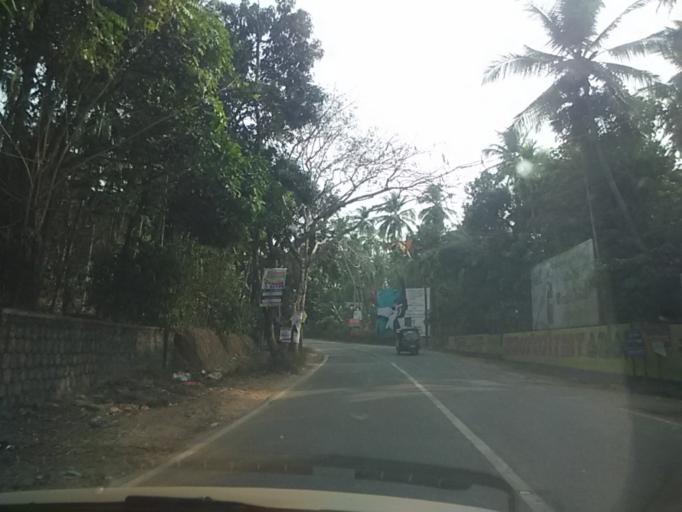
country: IN
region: Kerala
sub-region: Kozhikode
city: Naduvannur
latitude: 11.4747
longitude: 75.7747
